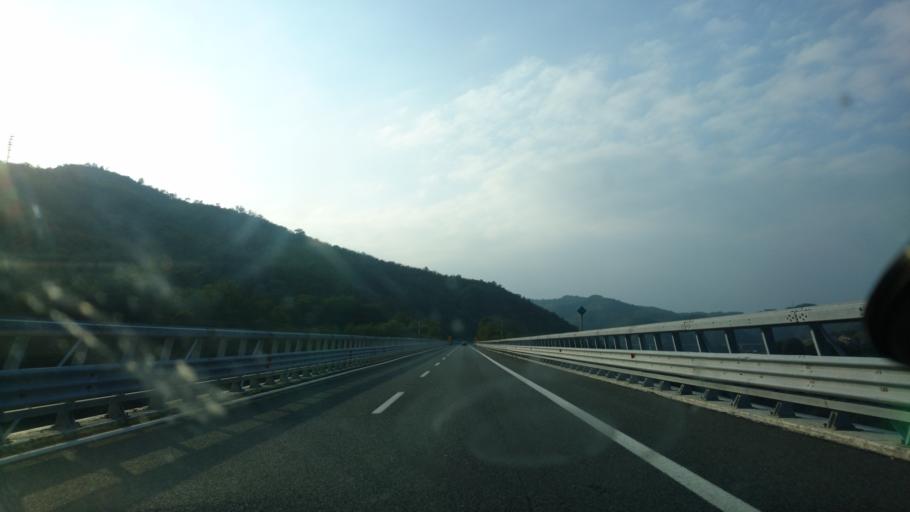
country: IT
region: Liguria
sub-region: Provincia di Savona
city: Quiliano
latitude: 44.3210
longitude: 8.3837
